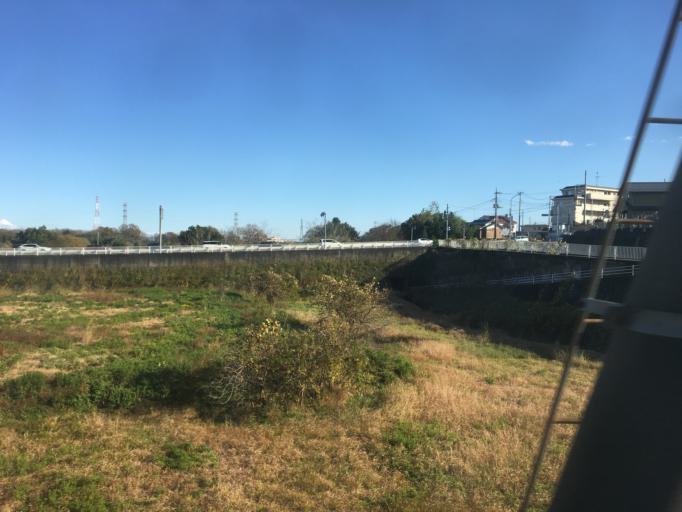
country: JP
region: Saitama
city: Sakado
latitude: 36.0090
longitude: 139.3980
